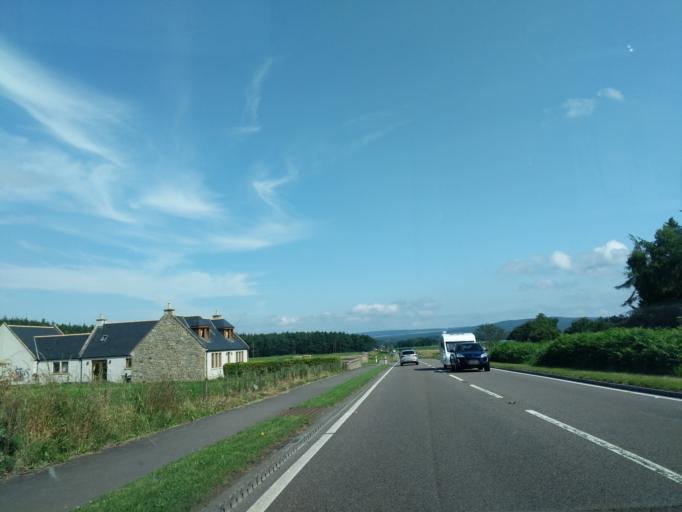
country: GB
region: Scotland
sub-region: Moray
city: Lhanbryd
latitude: 57.6271
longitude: -3.1611
